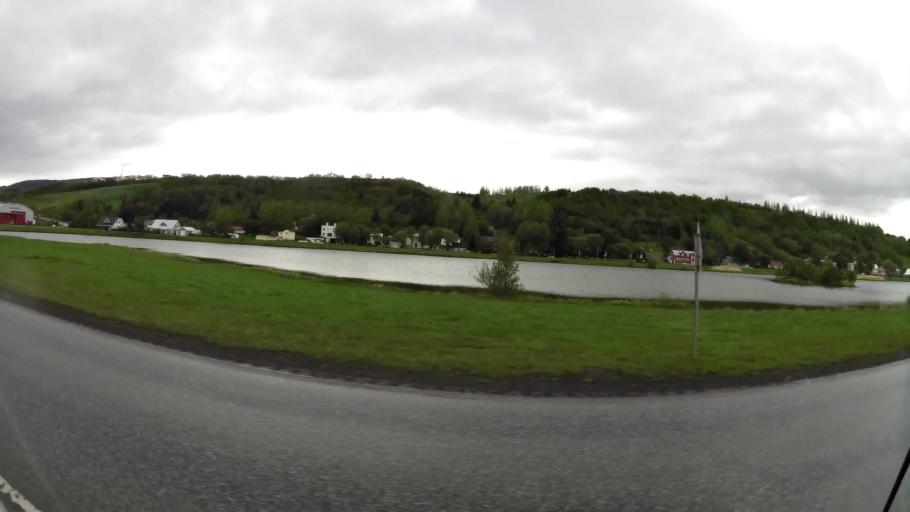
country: IS
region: Northeast
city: Akureyri
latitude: 65.6662
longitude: -18.0799
